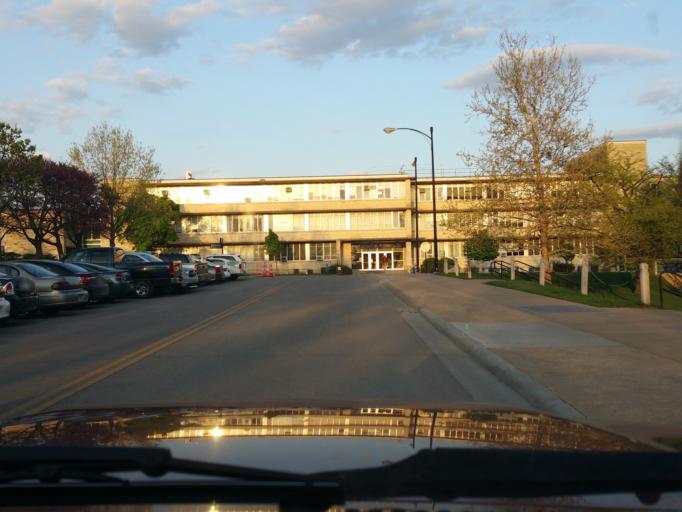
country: US
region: Kansas
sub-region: Riley County
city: Manhattan
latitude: 39.1896
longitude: -96.5842
